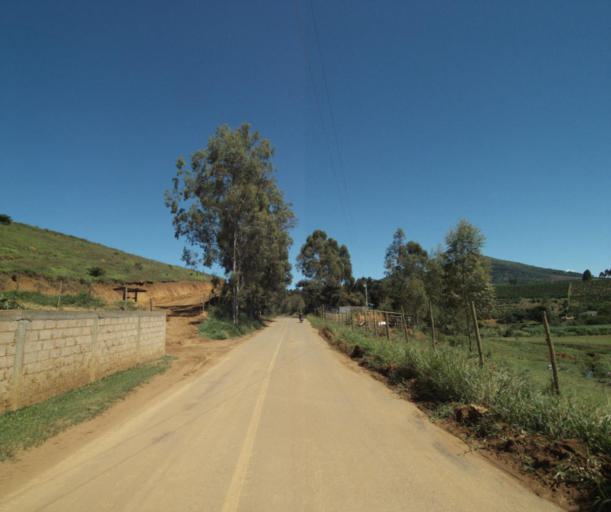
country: BR
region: Minas Gerais
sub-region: Espera Feliz
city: Espera Feliz
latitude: -20.5785
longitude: -41.8347
